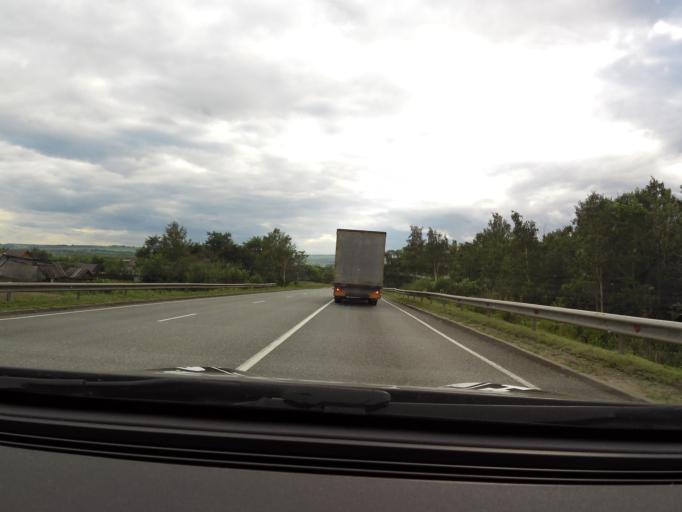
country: RU
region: Tatarstan
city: Sviyazhsk
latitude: 55.7163
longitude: 48.7217
